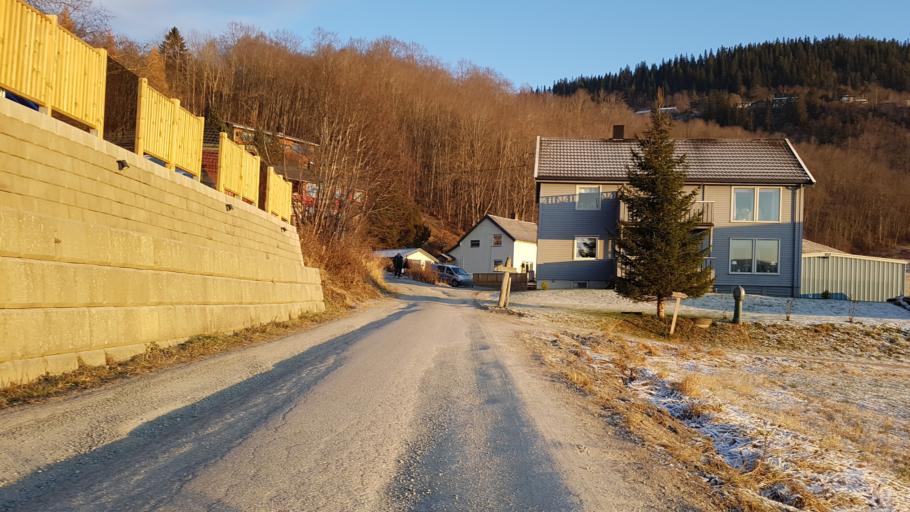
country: NO
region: Sor-Trondelag
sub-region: Melhus
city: Melhus
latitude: 63.2845
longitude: 10.2986
